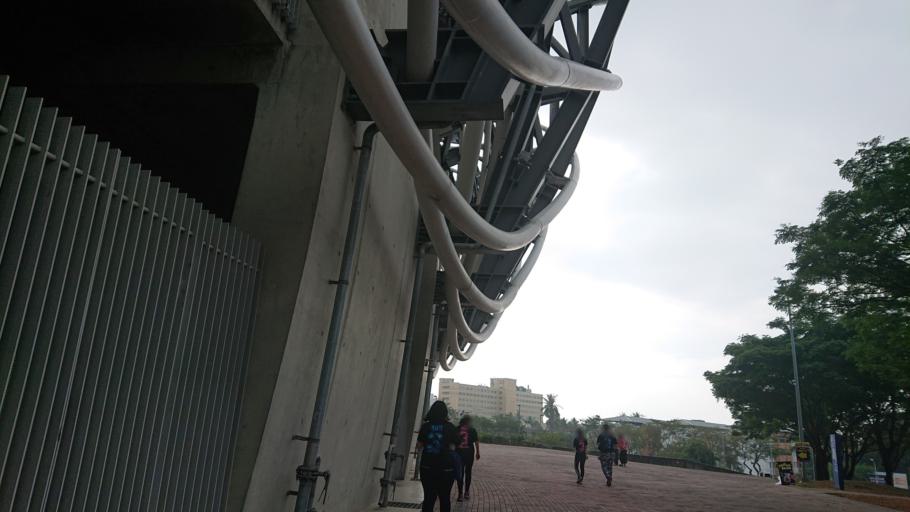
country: TW
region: Kaohsiung
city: Kaohsiung
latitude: 22.7044
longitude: 120.2938
